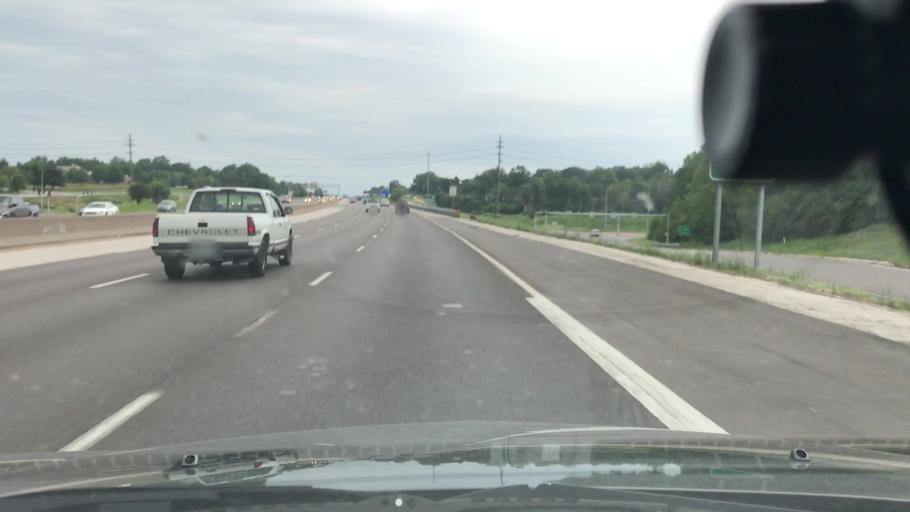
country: US
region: Missouri
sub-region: Saint Louis County
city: Creve Coeur
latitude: 38.6534
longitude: -90.4480
